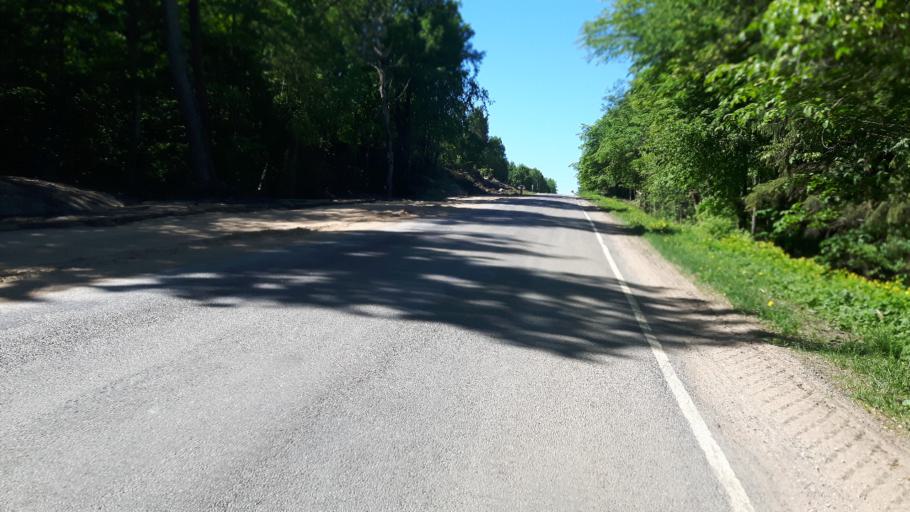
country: EE
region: Ida-Virumaa
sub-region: Narva-Joesuu linn
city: Narva-Joesuu
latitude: 59.4144
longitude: 27.9594
